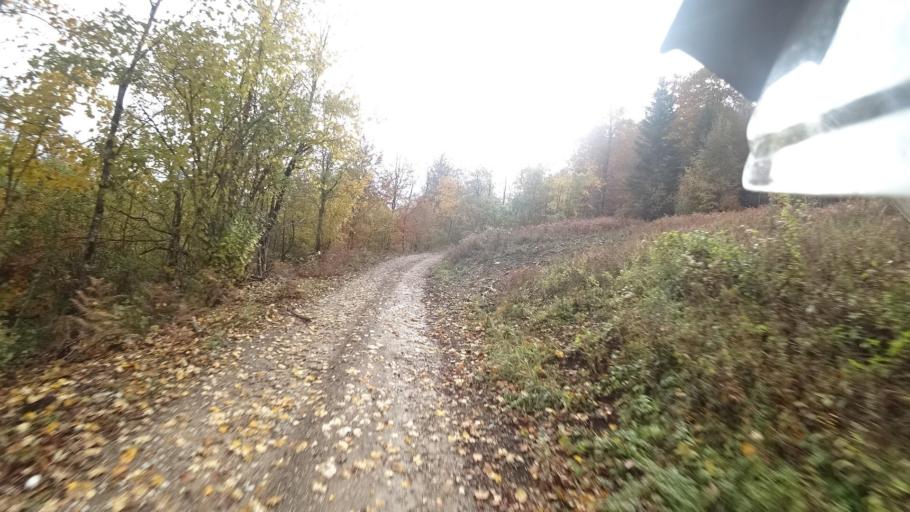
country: HR
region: Karlovacka
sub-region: Grad Ogulin
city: Ogulin
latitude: 45.1897
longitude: 15.1085
